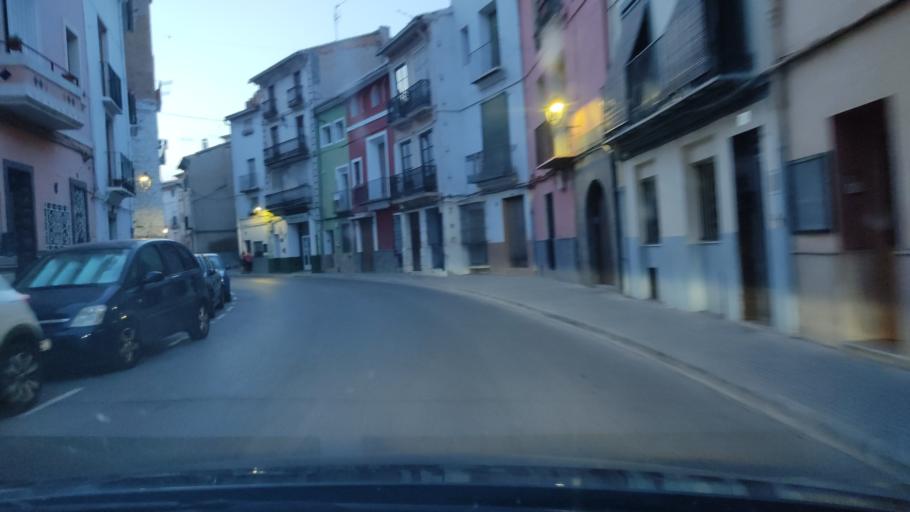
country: ES
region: Valencia
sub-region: Provincia de Castello
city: Jerica
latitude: 39.9117
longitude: -0.5705
